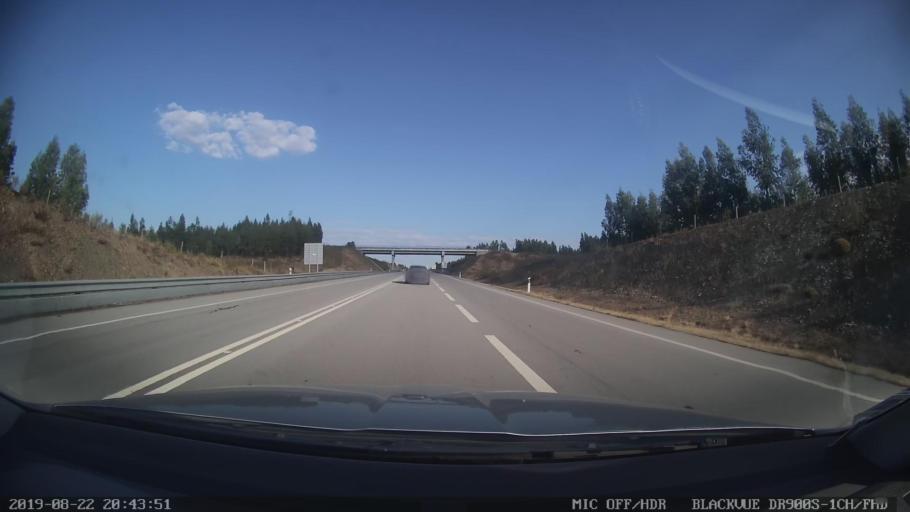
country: PT
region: Castelo Branco
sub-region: Proenca-A-Nova
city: Proenca-a-Nova
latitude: 39.7017
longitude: -7.8397
